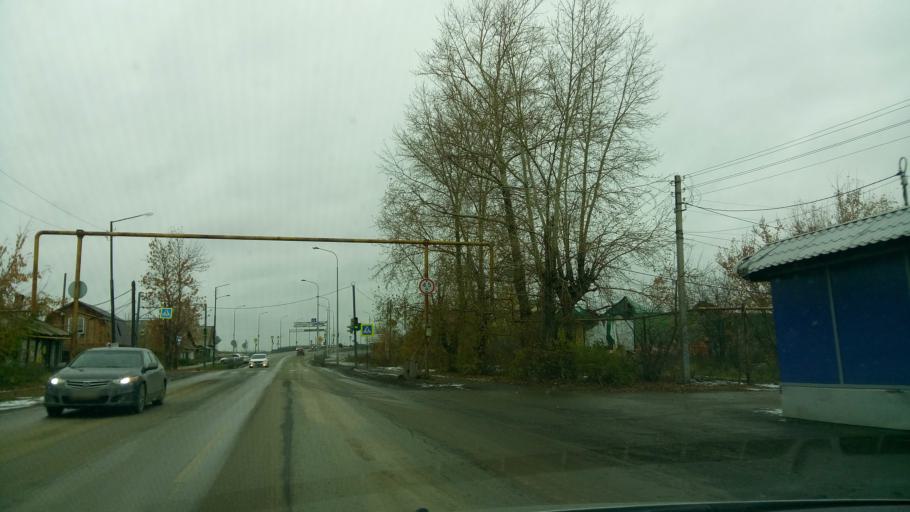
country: RU
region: Sverdlovsk
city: Verkhnyaya Pyshma
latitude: 56.9563
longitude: 60.5940
